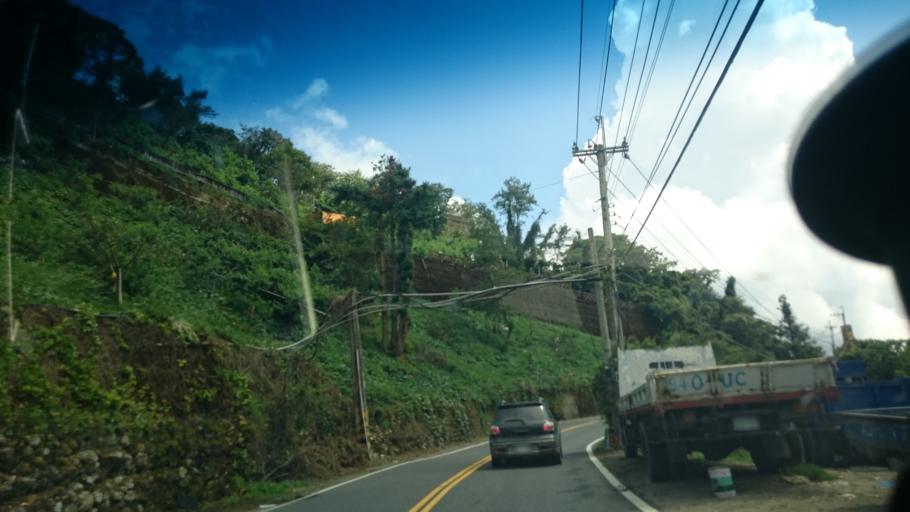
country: TW
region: Taiwan
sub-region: Nantou
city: Puli
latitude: 24.0385
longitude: 121.1453
